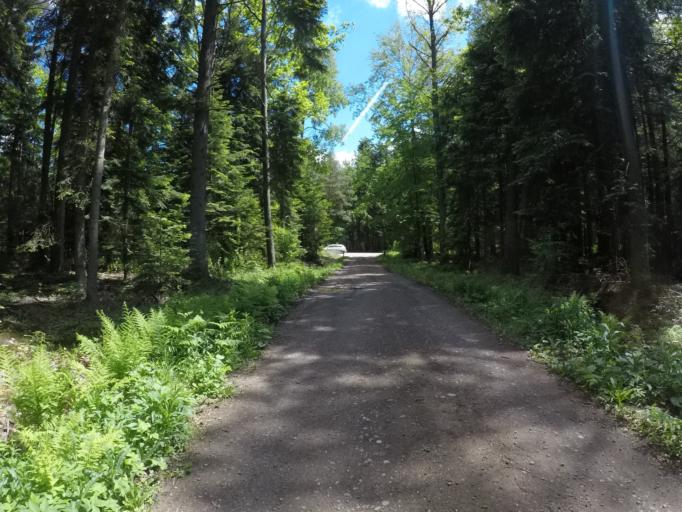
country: PL
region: Swietokrzyskie
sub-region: Powiat kielecki
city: Kostomloty Pierwsze
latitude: 50.9174
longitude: 20.6406
